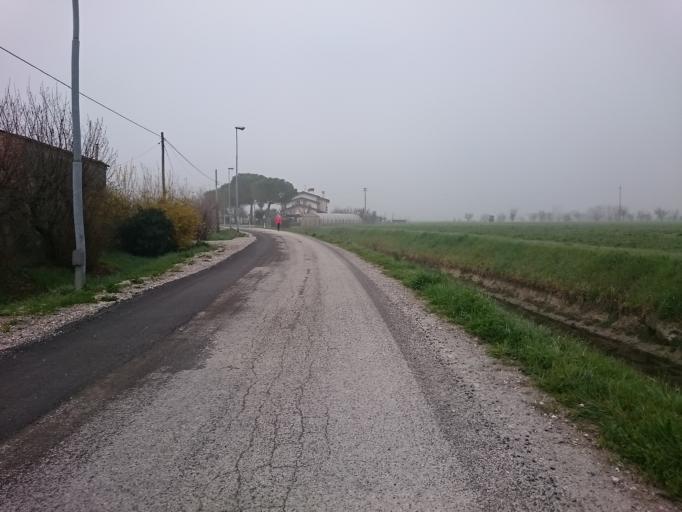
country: IT
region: Veneto
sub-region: Provincia di Padova
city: Masera di Padova
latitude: 45.3008
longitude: 11.8479
